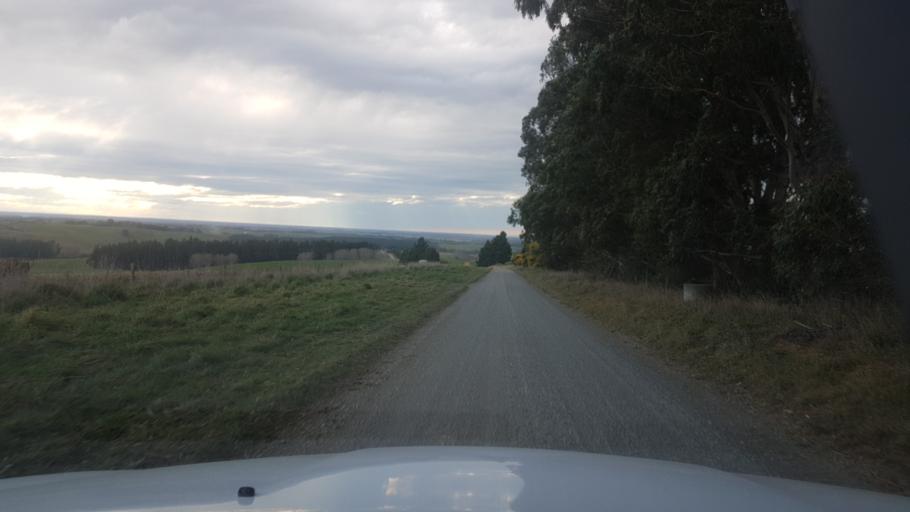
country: NZ
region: Canterbury
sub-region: Timaru District
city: Pleasant Point
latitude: -44.3453
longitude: 171.1354
